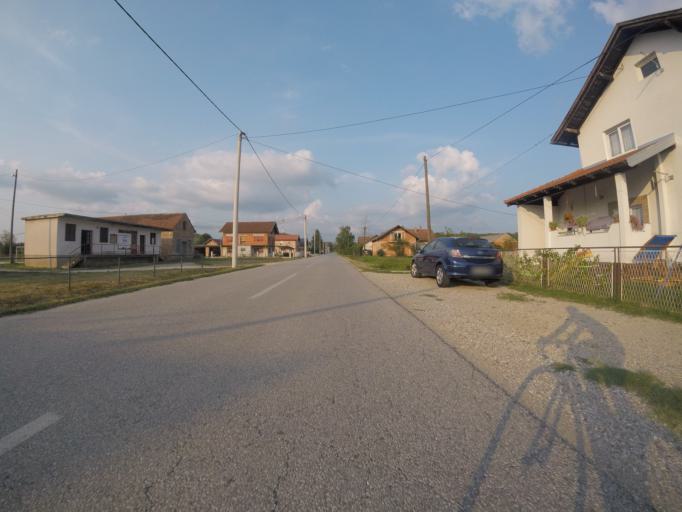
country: HR
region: Zagrebacka
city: Kuce
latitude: 45.7208
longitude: 16.2034
